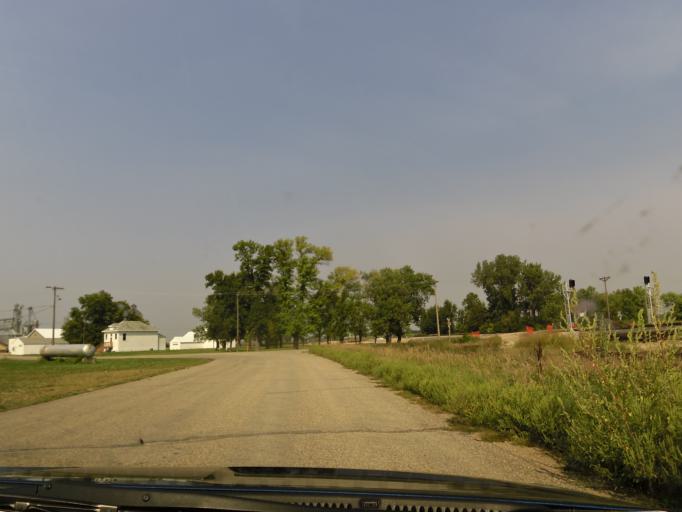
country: US
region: North Dakota
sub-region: Ransom County
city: Sheldon
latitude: 46.2663
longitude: -97.1283
